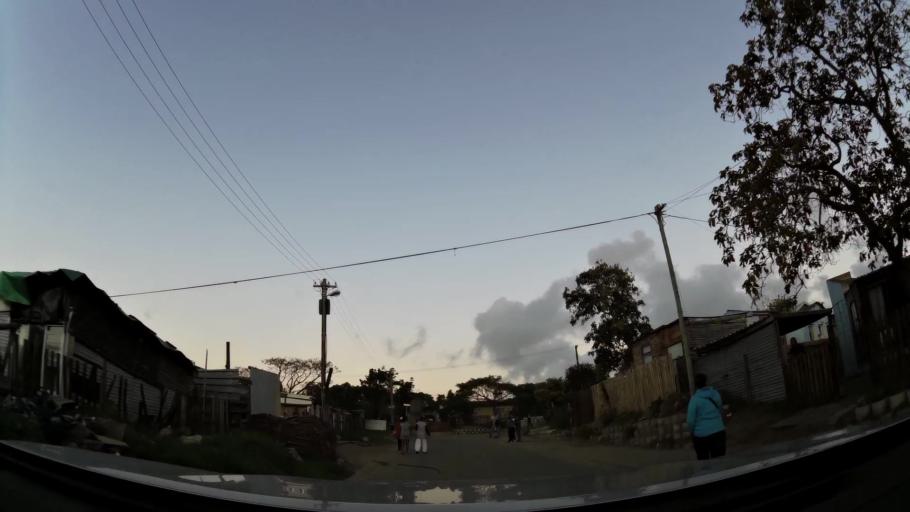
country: ZA
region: Western Cape
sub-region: Eden District Municipality
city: Knysna
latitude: -34.0266
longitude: 22.8129
